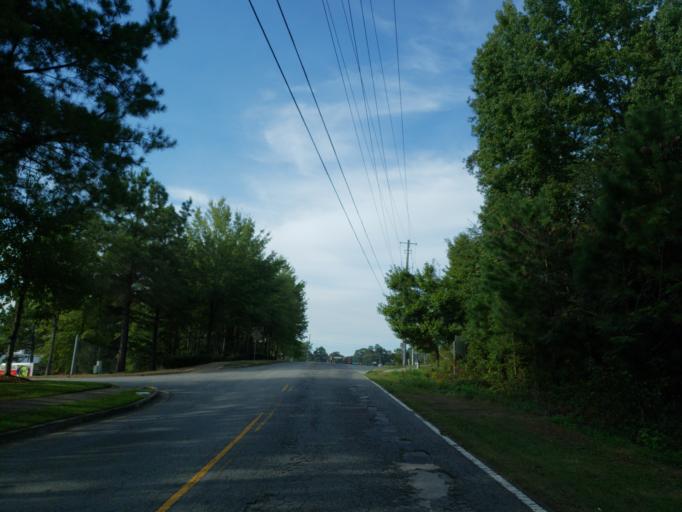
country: US
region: Georgia
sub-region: Cherokee County
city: Woodstock
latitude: 34.0846
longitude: -84.4986
